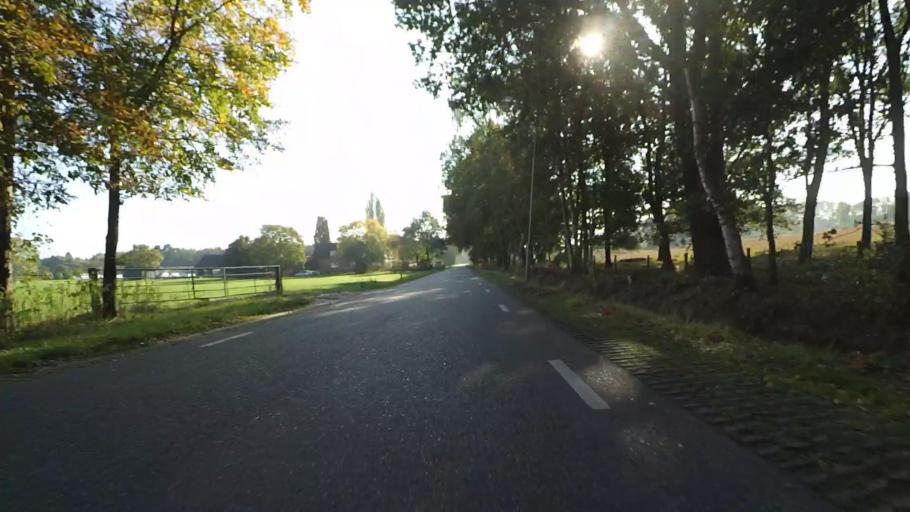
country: NL
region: Gelderland
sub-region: Gemeente Putten
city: Putten
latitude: 52.2472
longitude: 5.5505
